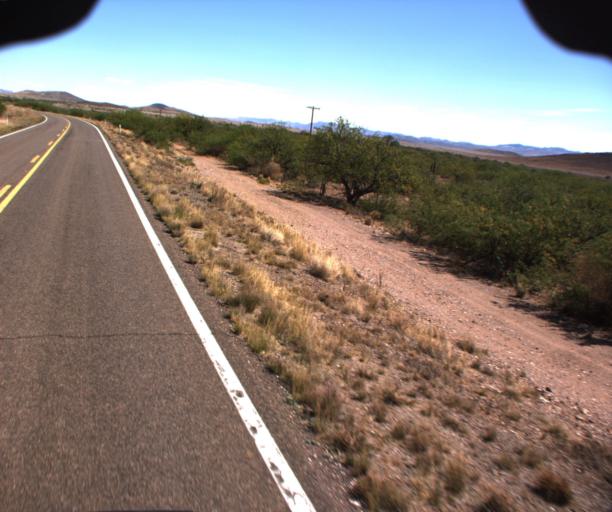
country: US
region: Arizona
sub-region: Cochise County
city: Douglas
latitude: 31.5120
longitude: -109.3109
